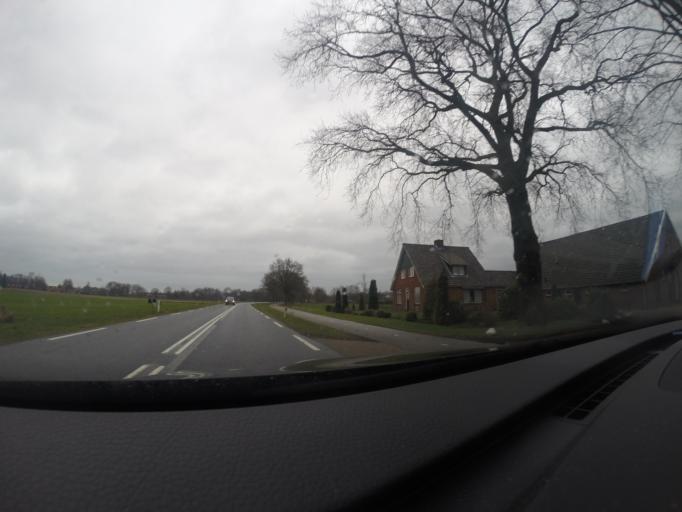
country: NL
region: Overijssel
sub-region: Gemeente Hof van Twente
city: Hengevelde
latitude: 52.2063
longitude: 6.6619
